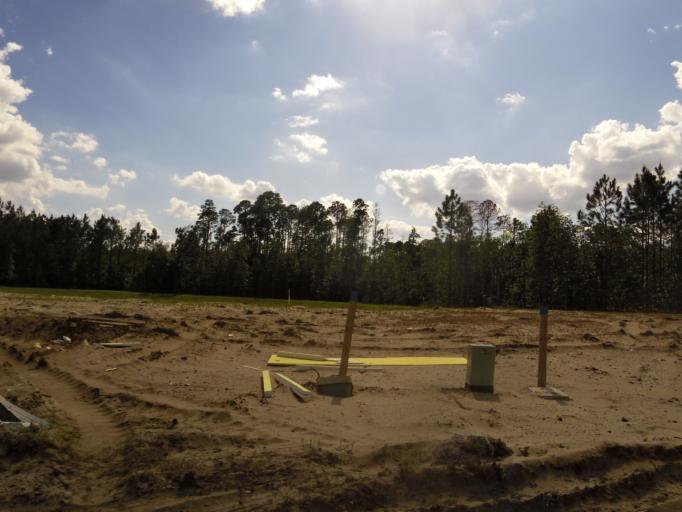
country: US
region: Florida
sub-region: Saint Johns County
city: Palm Valley
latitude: 30.2028
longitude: -81.5089
